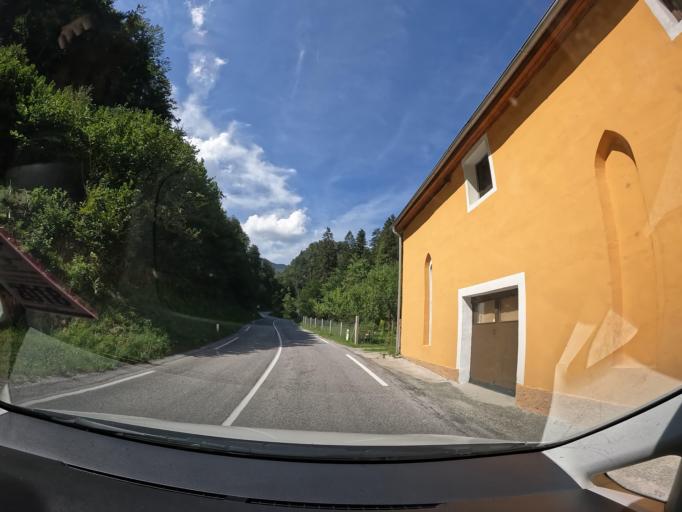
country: SI
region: Kranj
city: Golnik
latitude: 46.3832
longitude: 14.3806
